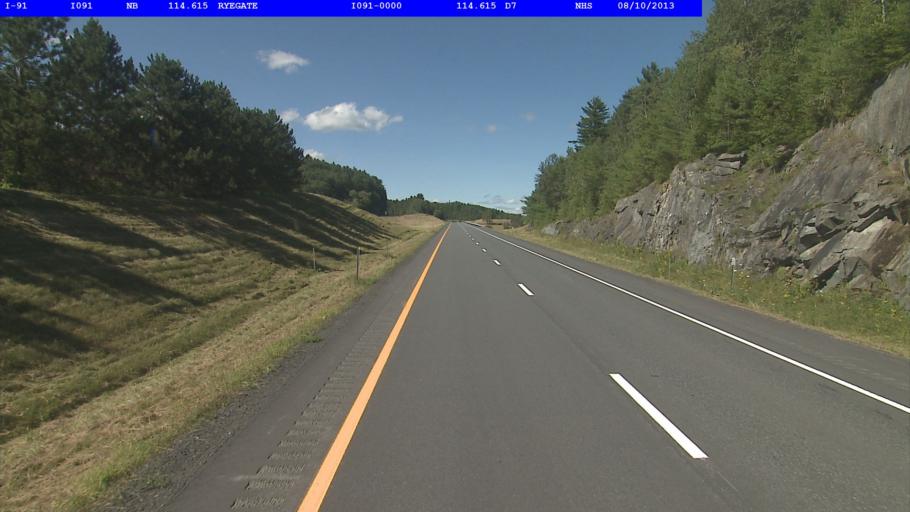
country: US
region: New Hampshire
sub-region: Grafton County
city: Woodsville
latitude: 44.2193
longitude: -72.0670
